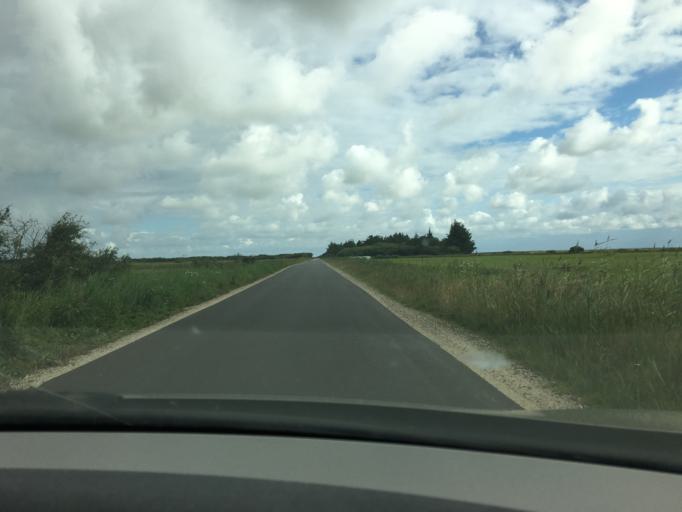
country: DK
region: Central Jutland
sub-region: Ringkobing-Skjern Kommune
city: Hvide Sande
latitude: 55.8292
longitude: 8.2162
